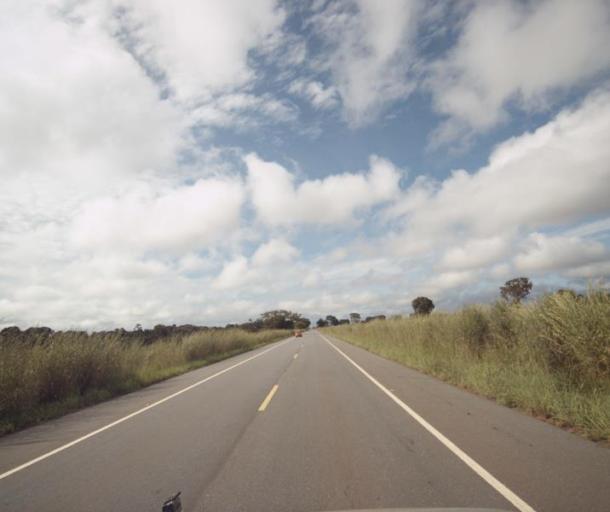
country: BR
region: Goias
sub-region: Barro Alto
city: Barro Alto
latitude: -15.2410
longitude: -48.6912
